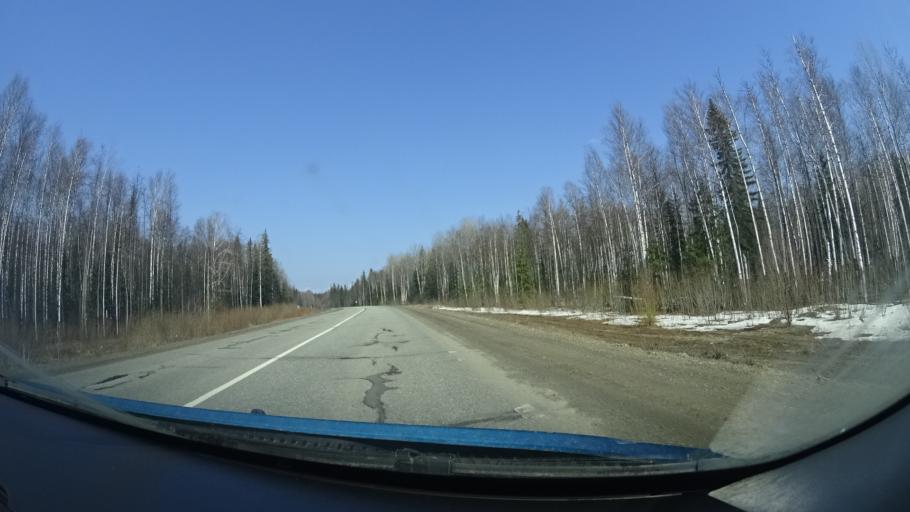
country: RU
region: Perm
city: Yugo-Kamskiy
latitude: 57.4991
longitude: 55.6878
